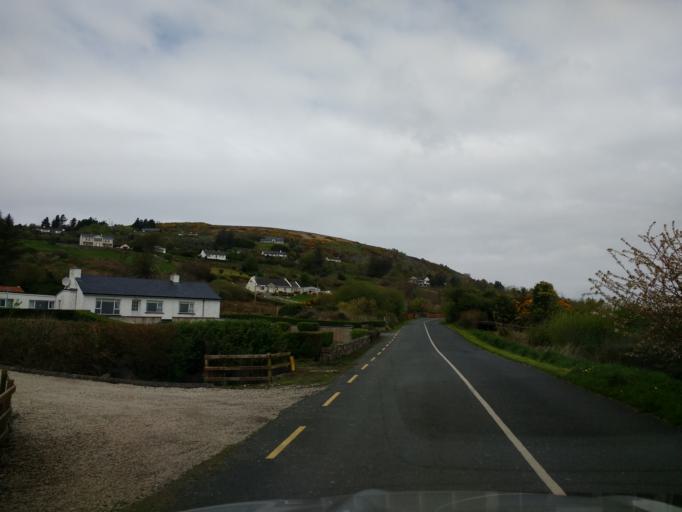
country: IE
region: Ulster
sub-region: County Donegal
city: Buncrana
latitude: 55.1447
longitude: -7.5446
